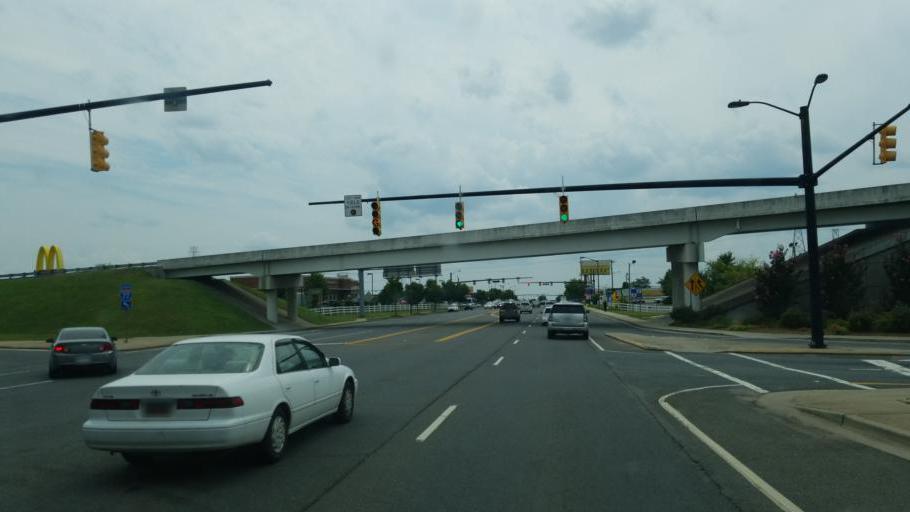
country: US
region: South Carolina
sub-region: York County
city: India Hook
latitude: 34.9735
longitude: -80.9869
